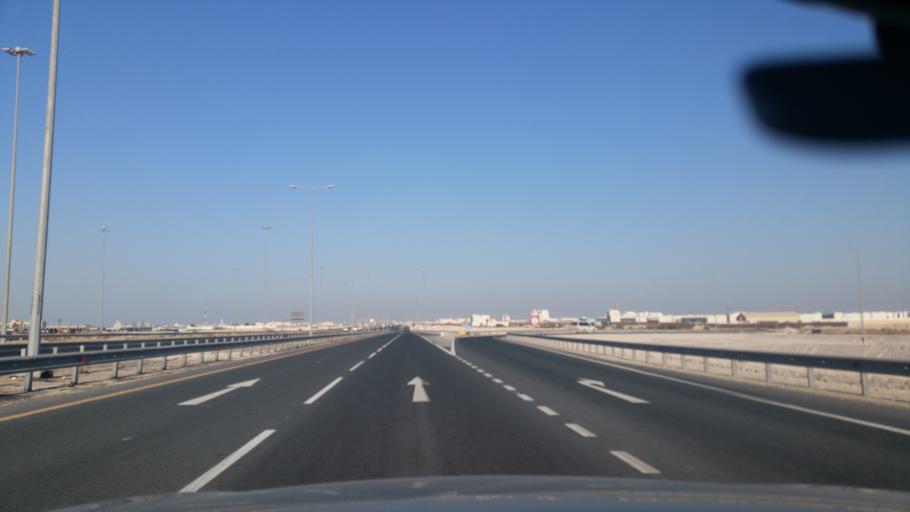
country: QA
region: Baladiyat ar Rayyan
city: Ar Rayyan
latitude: 25.1775
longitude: 51.3424
